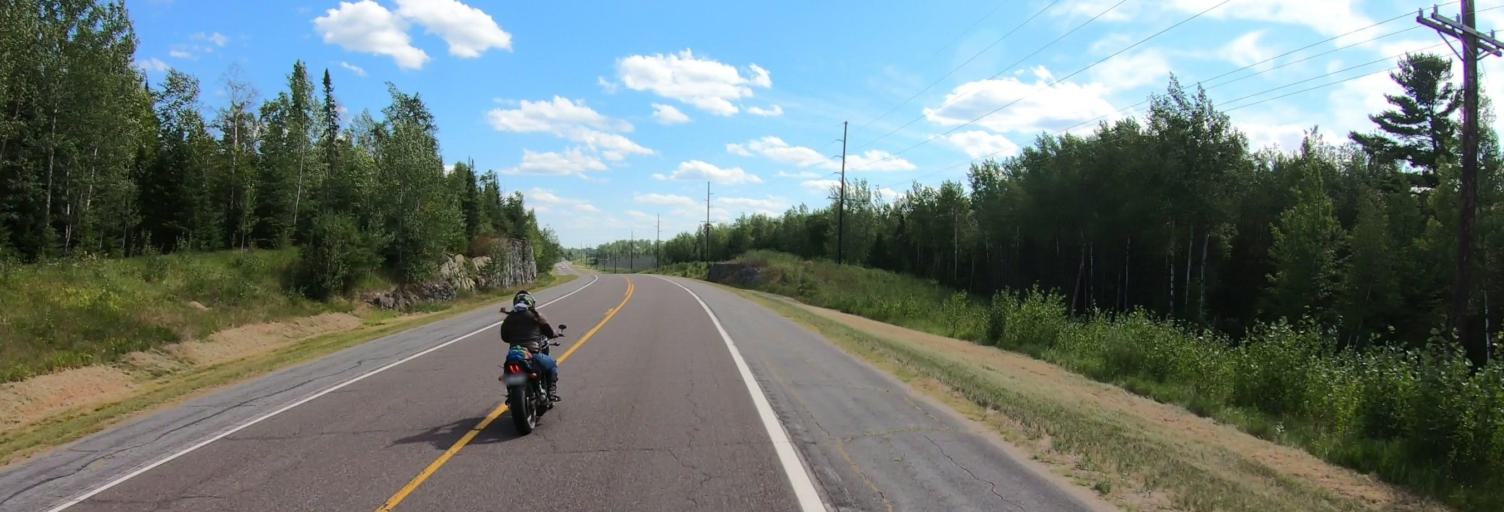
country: US
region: Minnesota
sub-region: Saint Louis County
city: Aurora
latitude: 47.8257
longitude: -92.3727
